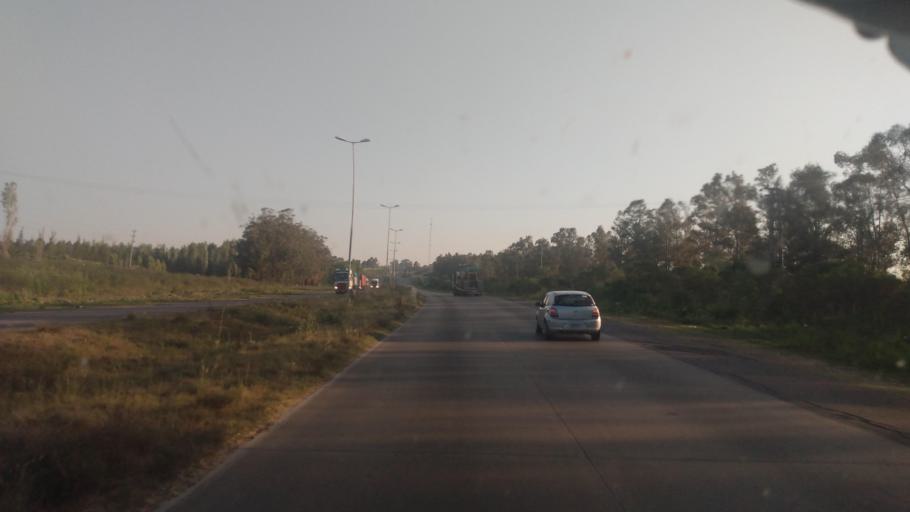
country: AR
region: Buenos Aires
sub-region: Partido de Campana
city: Campana
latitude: -34.2198
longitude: -58.9588
